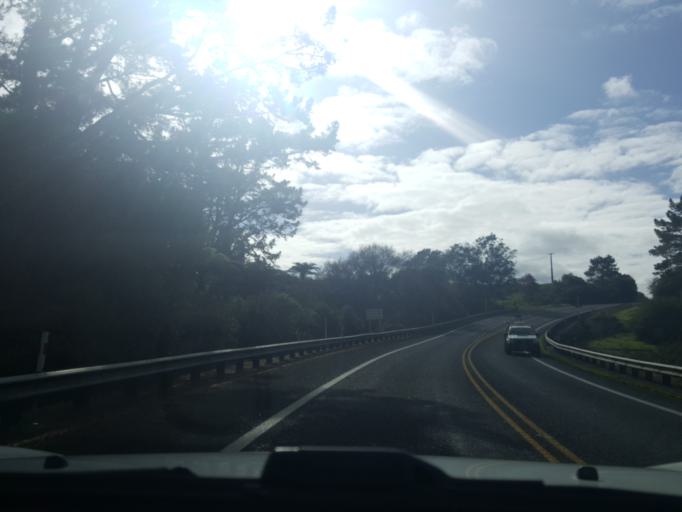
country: NZ
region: Waikato
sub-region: Hauraki District
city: Waihi
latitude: -37.4118
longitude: 175.7971
